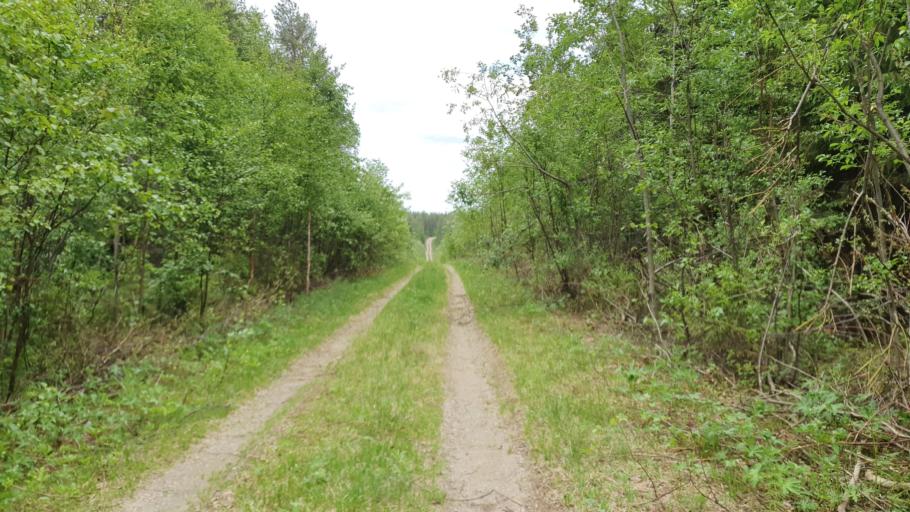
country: FI
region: Kainuu
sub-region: Kehys-Kainuu
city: Kuhmo
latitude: 64.4391
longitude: 29.6881
